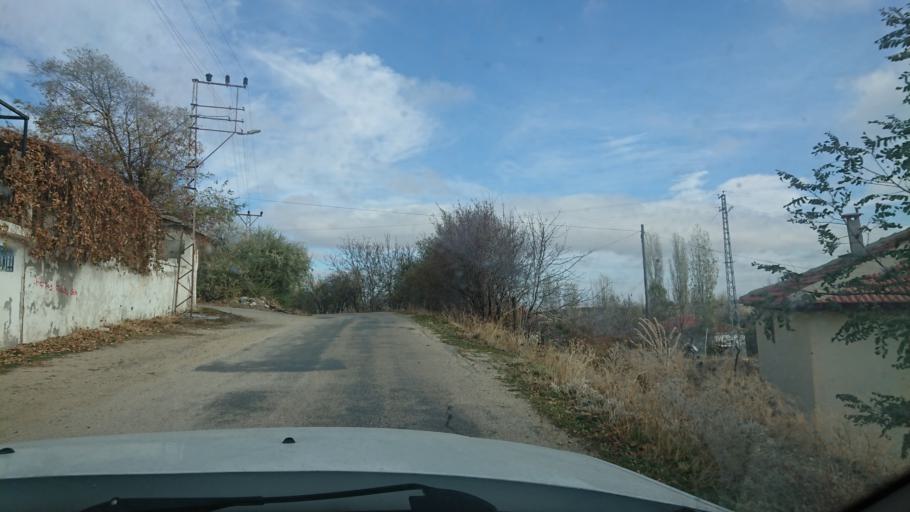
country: TR
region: Aksaray
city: Ortakoy
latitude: 38.8074
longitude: 33.9835
